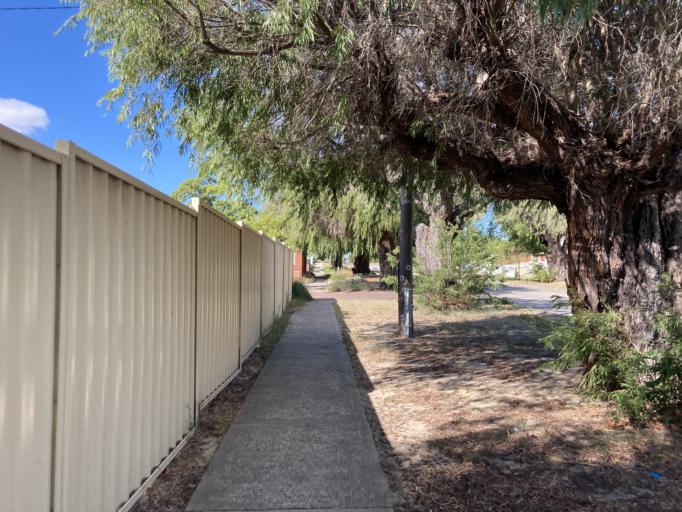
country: AU
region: Western Australia
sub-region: Melville
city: Palmyra
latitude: -32.0412
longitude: 115.7909
